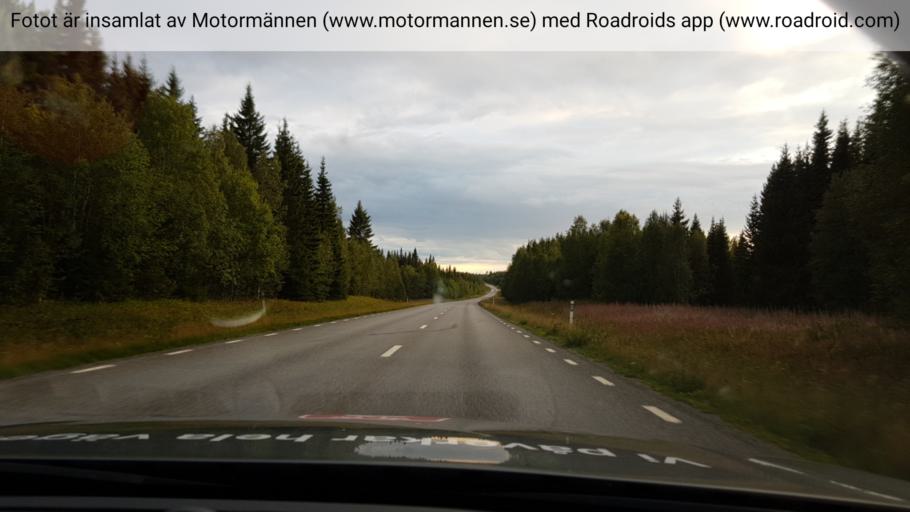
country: SE
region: Jaemtland
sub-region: OEstersunds Kommun
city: Lit
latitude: 63.4537
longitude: 15.1665
